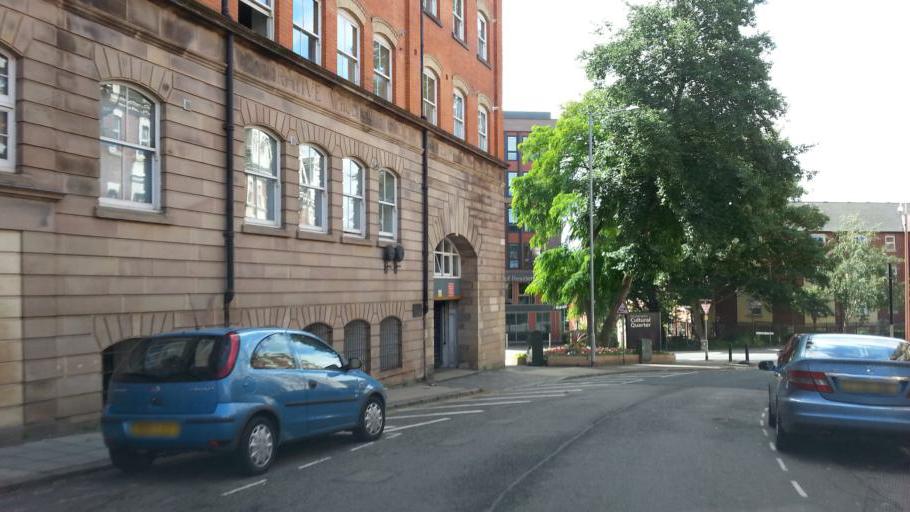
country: GB
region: England
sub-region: Northamptonshire
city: Northampton
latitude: 52.2356
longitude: -0.8943
